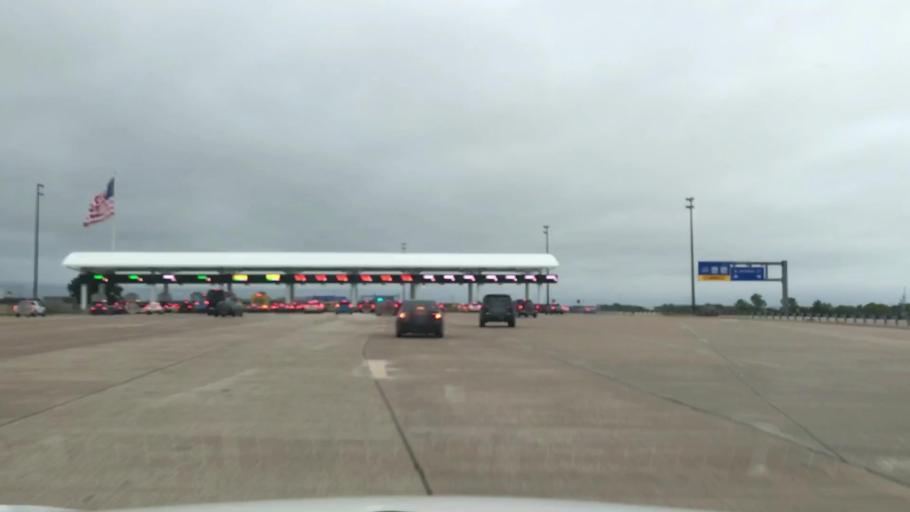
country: US
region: Texas
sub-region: Tarrant County
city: Grapevine
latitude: 32.9213
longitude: -97.0395
